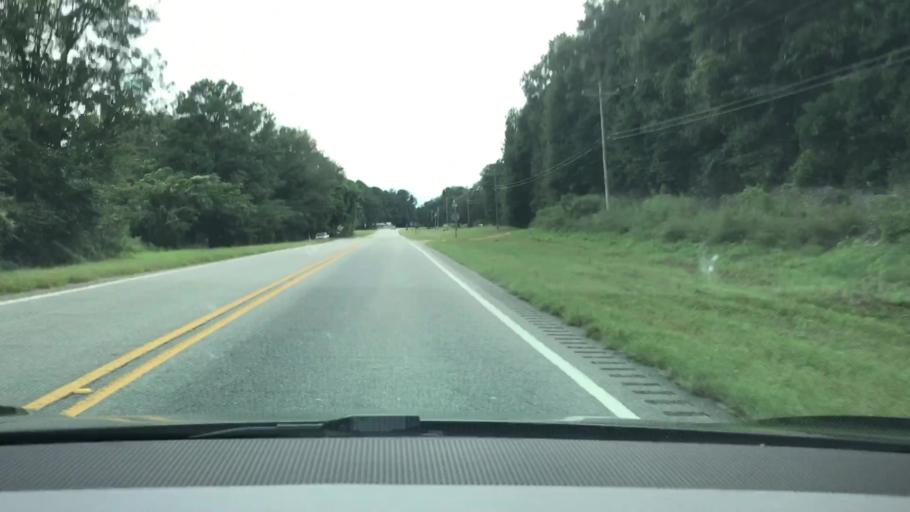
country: US
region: Alabama
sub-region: Coffee County
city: Elba
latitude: 31.5765
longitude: -85.9982
